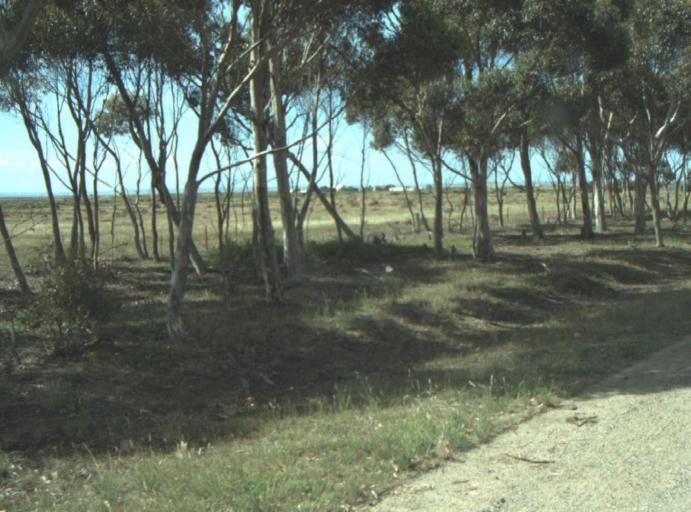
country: AU
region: Victoria
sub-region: Greater Geelong
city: Lara
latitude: -38.0615
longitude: 144.4265
